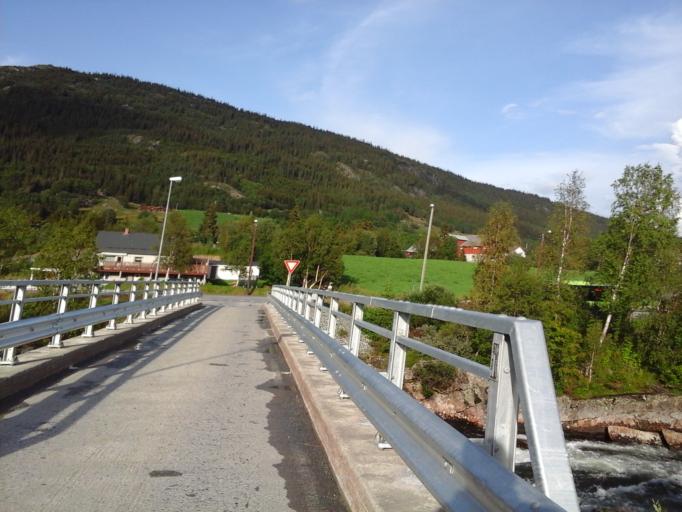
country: NO
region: Buskerud
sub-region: Hemsedal
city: Troim
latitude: 60.8446
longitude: 8.6195
